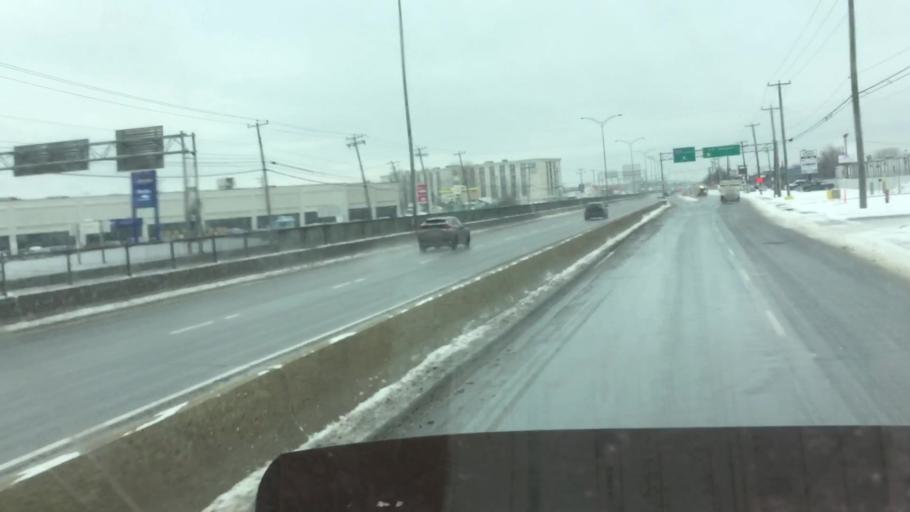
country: CA
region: Quebec
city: Dorval
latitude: 45.4640
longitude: -73.7209
